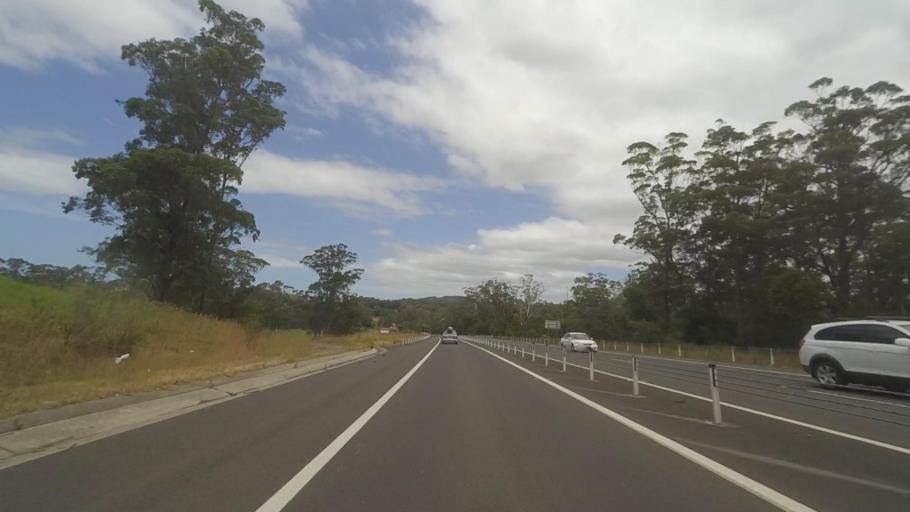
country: AU
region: New South Wales
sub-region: Shoalhaven Shire
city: Milton
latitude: -35.2105
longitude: 150.4370
